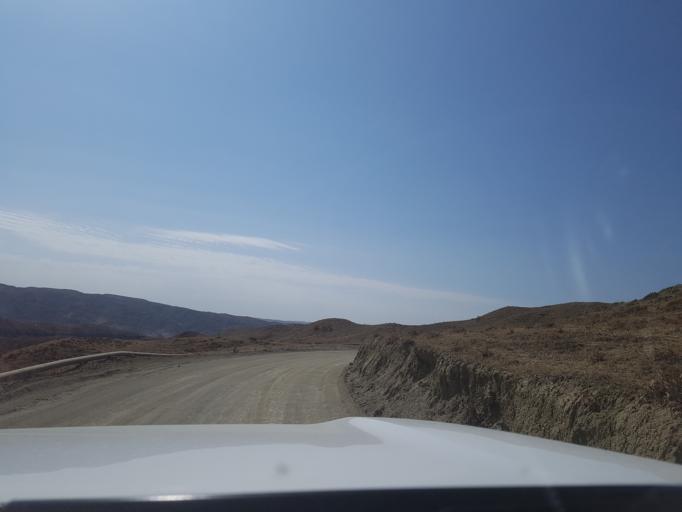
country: TM
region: Ahal
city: Baharly
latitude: 38.2434
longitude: 56.8904
